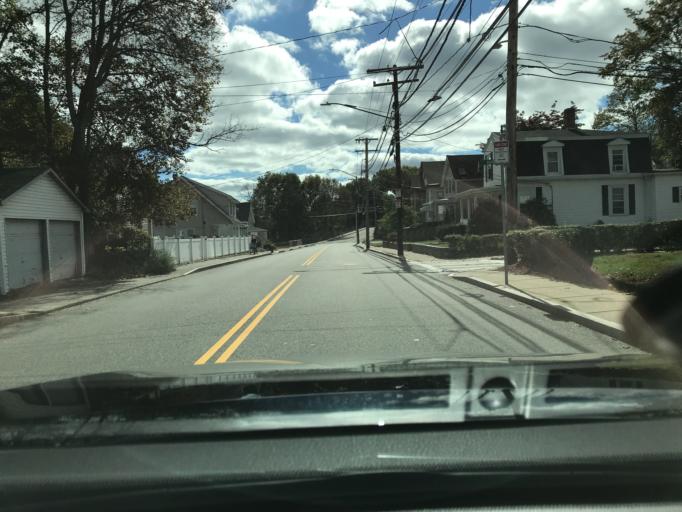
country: US
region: Massachusetts
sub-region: Norfolk County
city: Dedham
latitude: 42.2817
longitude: -71.1688
